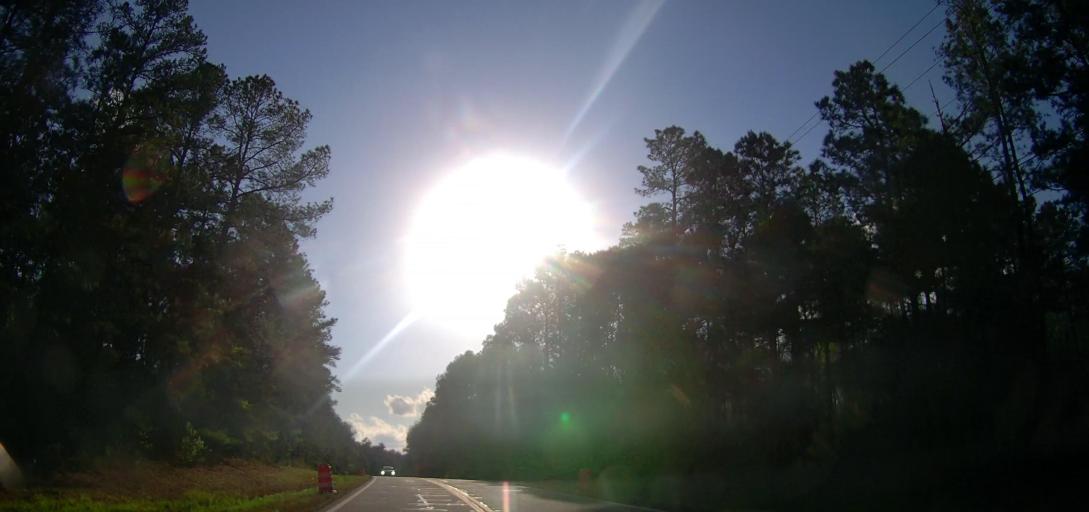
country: US
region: Georgia
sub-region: Baldwin County
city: Milledgeville
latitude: 33.1281
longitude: -83.3083
